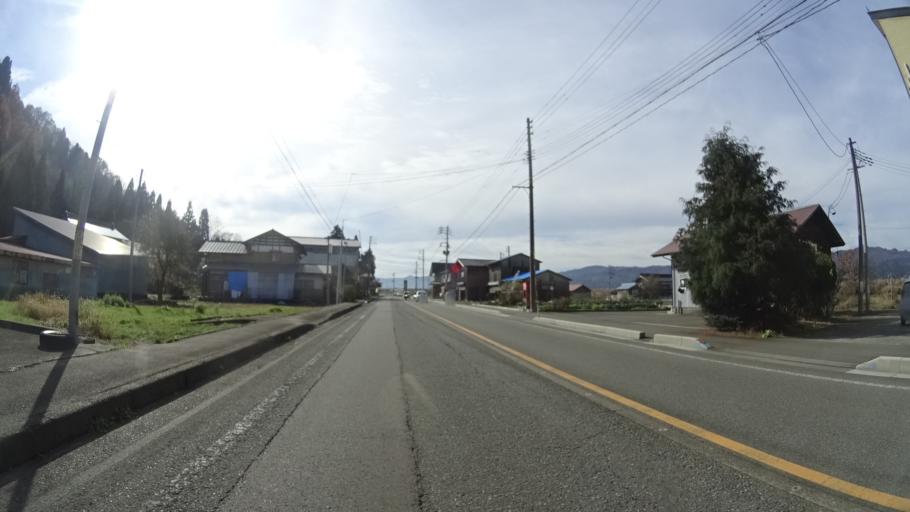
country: JP
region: Niigata
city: Muikamachi
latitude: 37.1201
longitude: 138.9234
